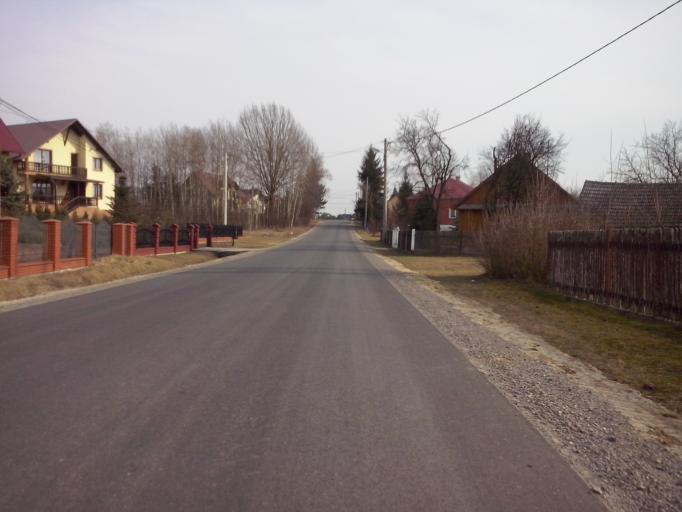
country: PL
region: Subcarpathian Voivodeship
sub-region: Powiat nizanski
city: Krzeszow
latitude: 50.4246
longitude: 22.3576
